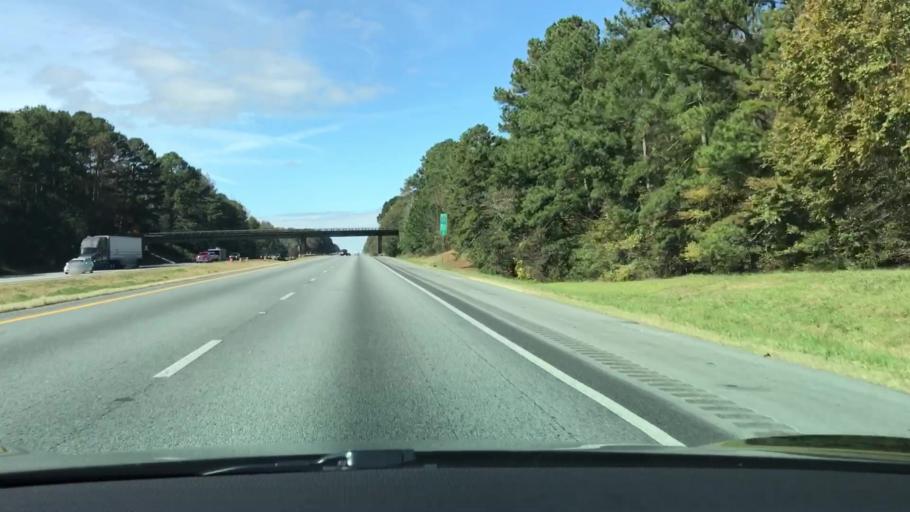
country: US
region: Georgia
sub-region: Morgan County
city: Madison
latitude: 33.5807
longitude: -83.5864
